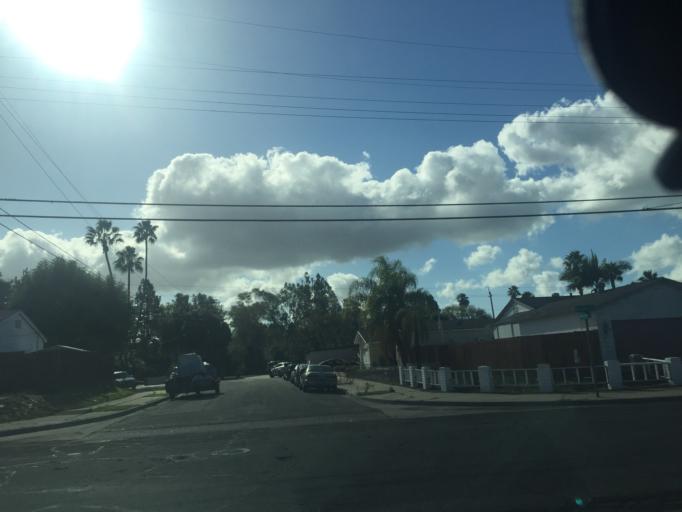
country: US
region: California
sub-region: San Diego County
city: La Mesa
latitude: 32.7889
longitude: -117.0949
